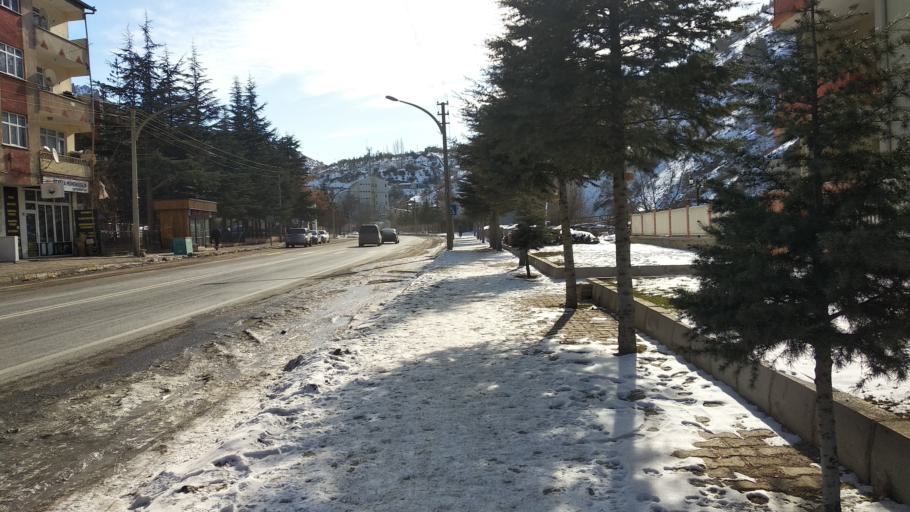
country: TR
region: Gumushane
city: Gumushkhane
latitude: 40.4490
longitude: 39.4963
